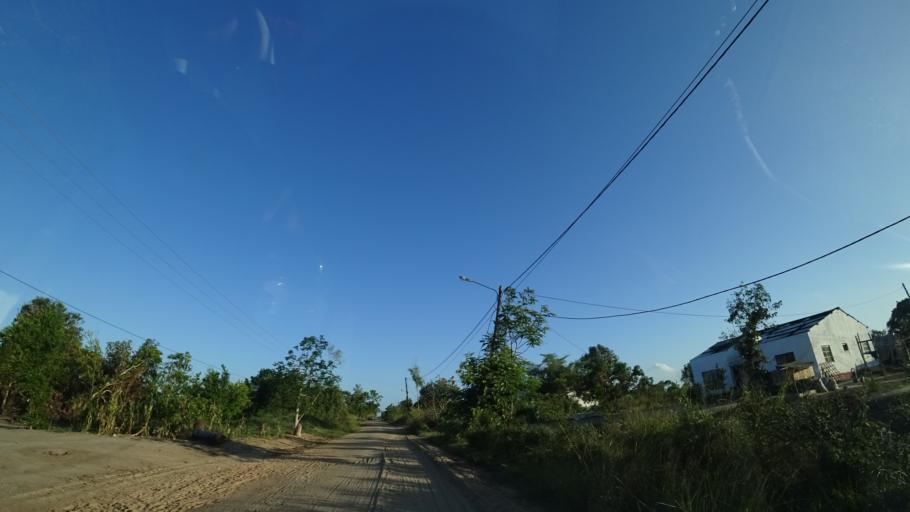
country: MZ
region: Sofala
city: Dondo
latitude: -19.3955
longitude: 34.7088
